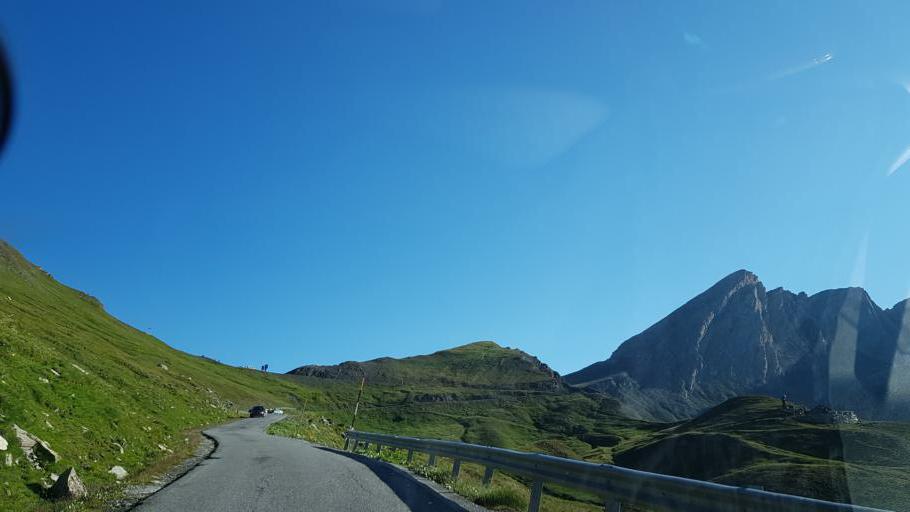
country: IT
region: Piedmont
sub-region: Provincia di Cuneo
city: Pontechianale
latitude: 44.6797
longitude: 6.9783
